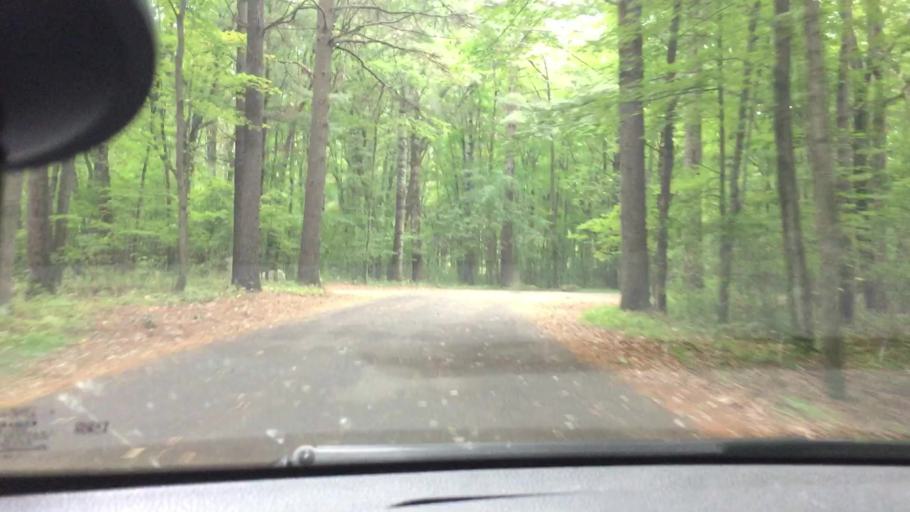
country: US
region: Wisconsin
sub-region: Chippewa County
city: Chippewa Falls
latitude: 44.9577
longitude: -91.4013
